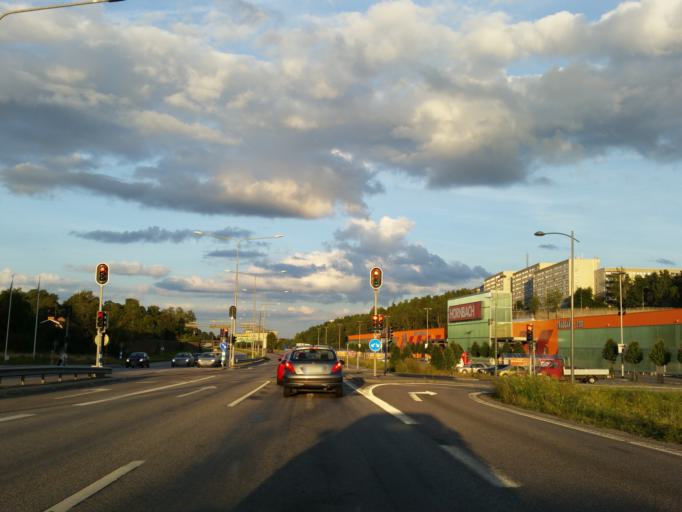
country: SE
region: Stockholm
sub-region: Stockholms Kommun
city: Kista
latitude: 59.3799
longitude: 17.9534
